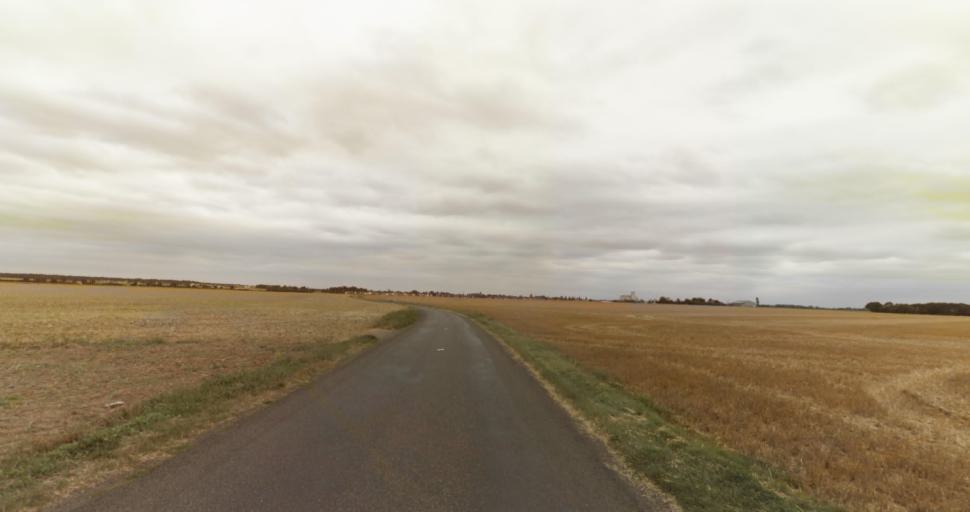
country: FR
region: Haute-Normandie
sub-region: Departement de l'Eure
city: Marcilly-sur-Eure
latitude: 48.9230
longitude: 1.2718
